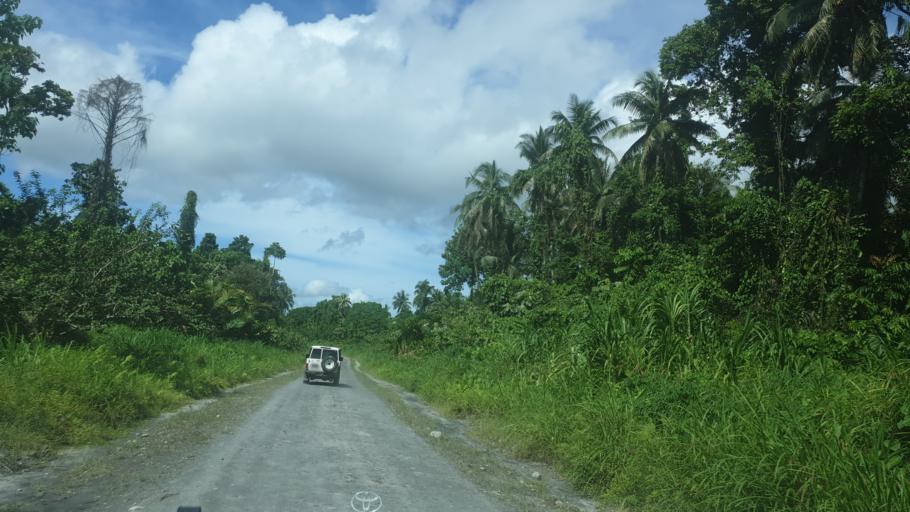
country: PG
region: Bougainville
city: Panguna
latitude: -6.5555
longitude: 155.3536
